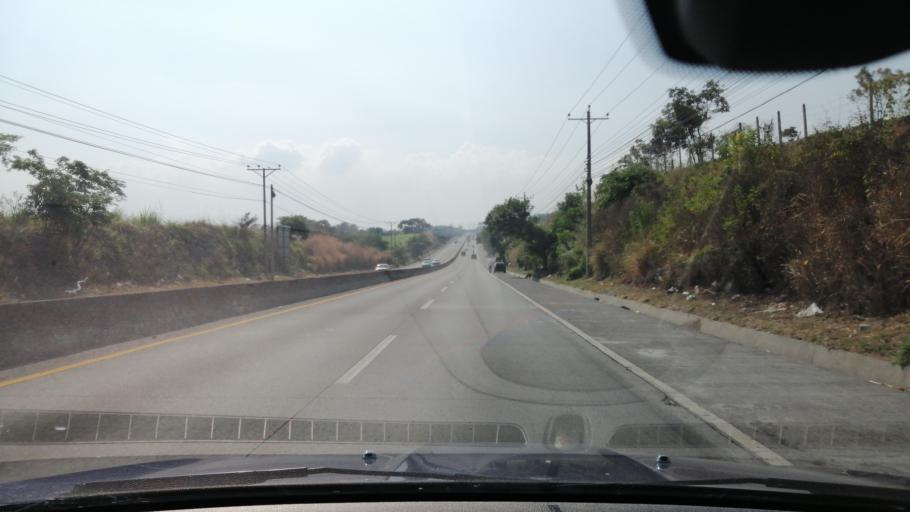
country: SV
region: San Salvador
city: Apopa
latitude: 13.7930
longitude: -89.2244
